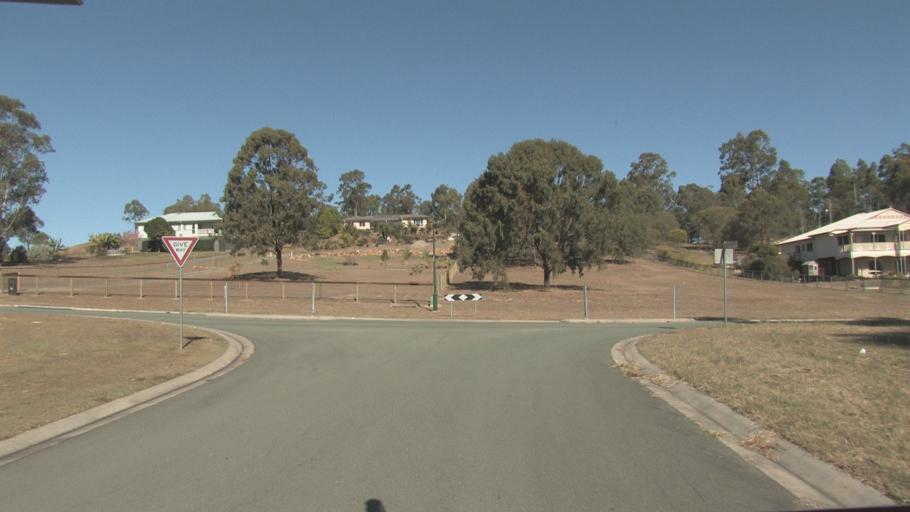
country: AU
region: Queensland
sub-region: Logan
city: Cedar Vale
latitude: -27.8686
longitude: 153.0337
